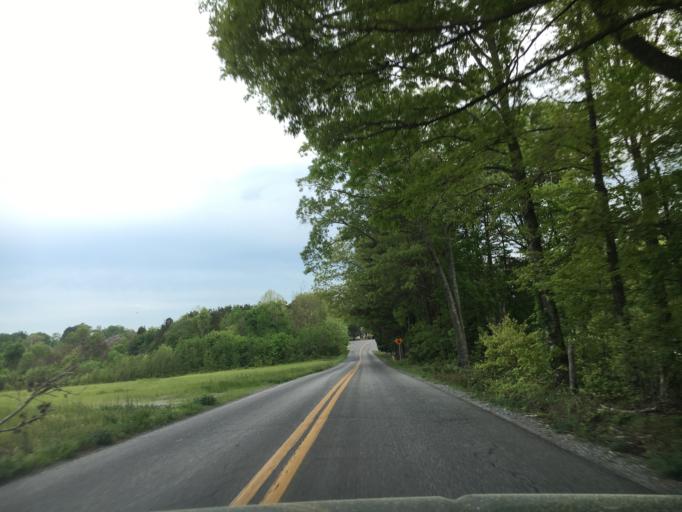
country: US
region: Virginia
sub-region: Campbell County
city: Brookneal
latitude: 36.9221
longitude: -78.9478
